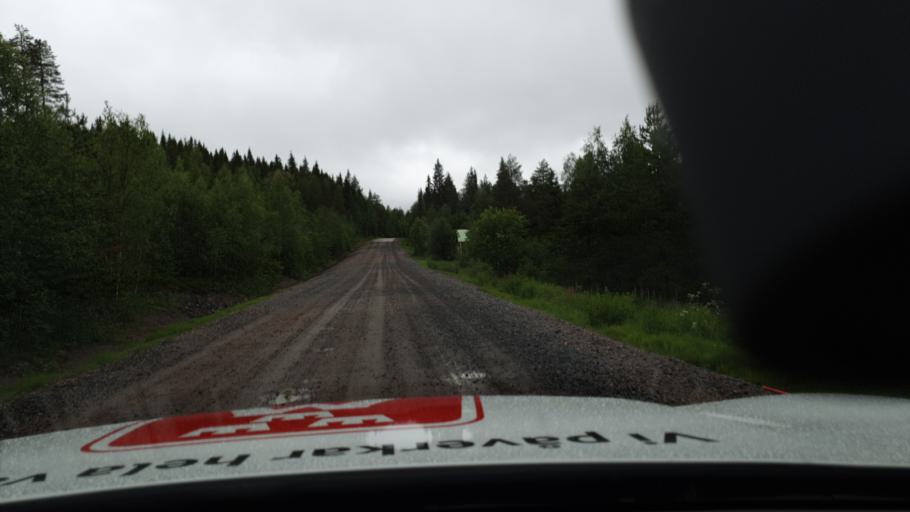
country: SE
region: Norrbotten
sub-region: Overtornea Kommun
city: OEvertornea
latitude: 66.4209
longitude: 23.5621
